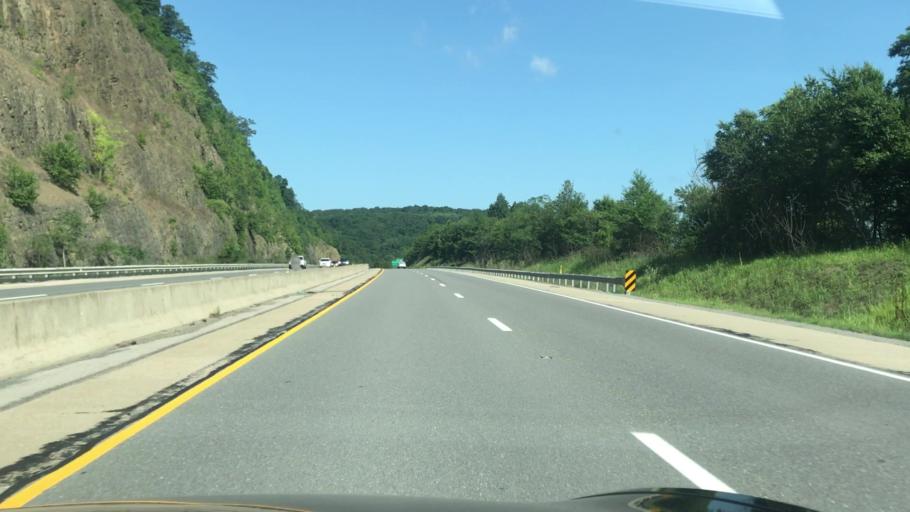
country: US
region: Pennsylvania
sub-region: Lycoming County
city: Garden View
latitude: 41.2732
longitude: -77.0583
